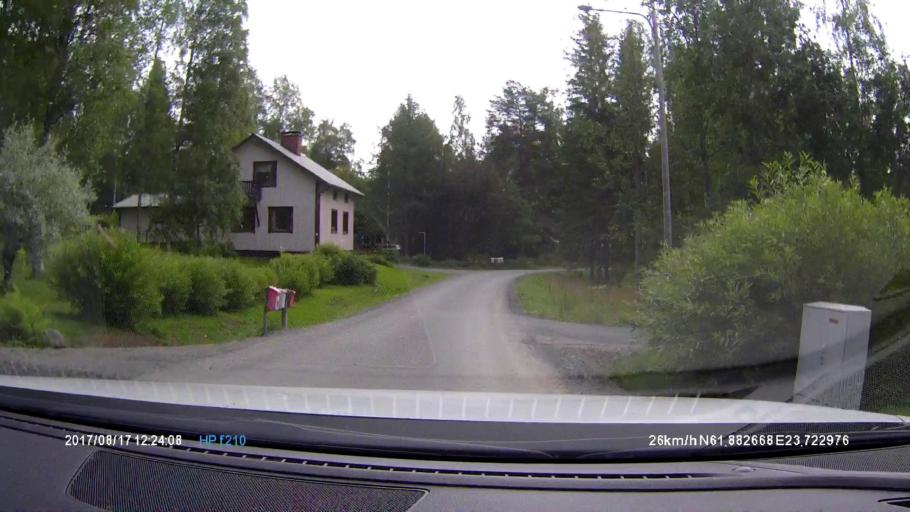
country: FI
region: Pirkanmaa
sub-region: Tampere
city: Kuru
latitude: 61.8827
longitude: 23.7233
